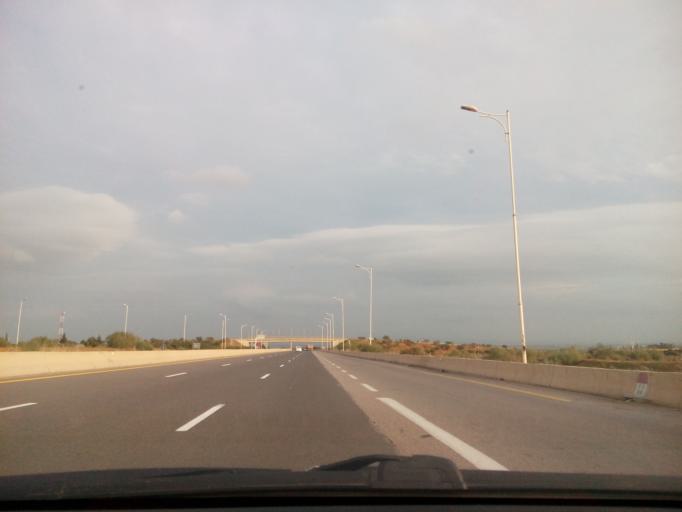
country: DZ
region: Relizane
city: Relizane
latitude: 35.7896
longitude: 0.4069
